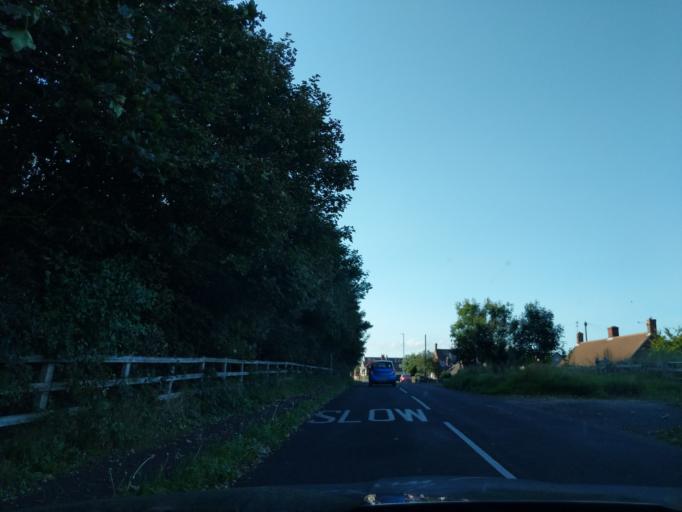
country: GB
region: England
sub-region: Northumberland
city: Lynemouth
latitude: 55.2111
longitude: -1.5355
